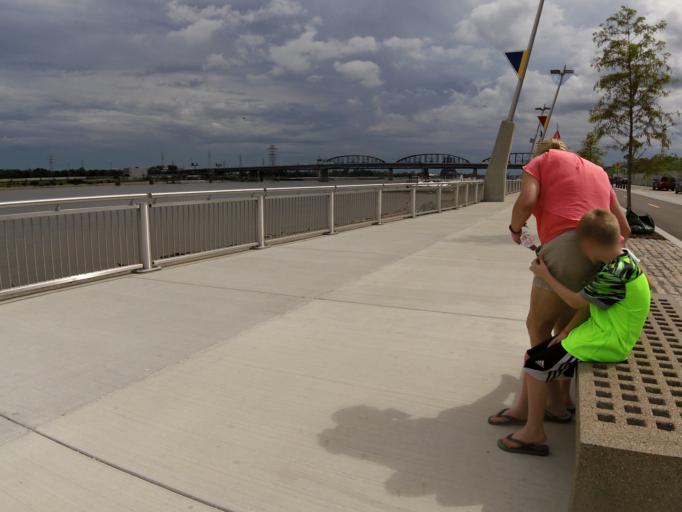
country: US
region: Missouri
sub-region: City of Saint Louis
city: St. Louis
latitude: 38.6253
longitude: -90.1834
